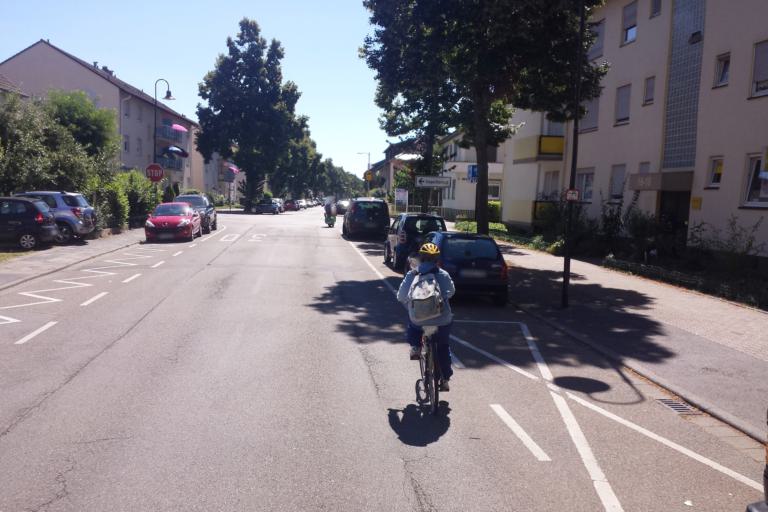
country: DE
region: Baden-Wuerttemberg
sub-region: Karlsruhe Region
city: Edingen-Neckarhausen
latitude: 49.4435
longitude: 8.5816
